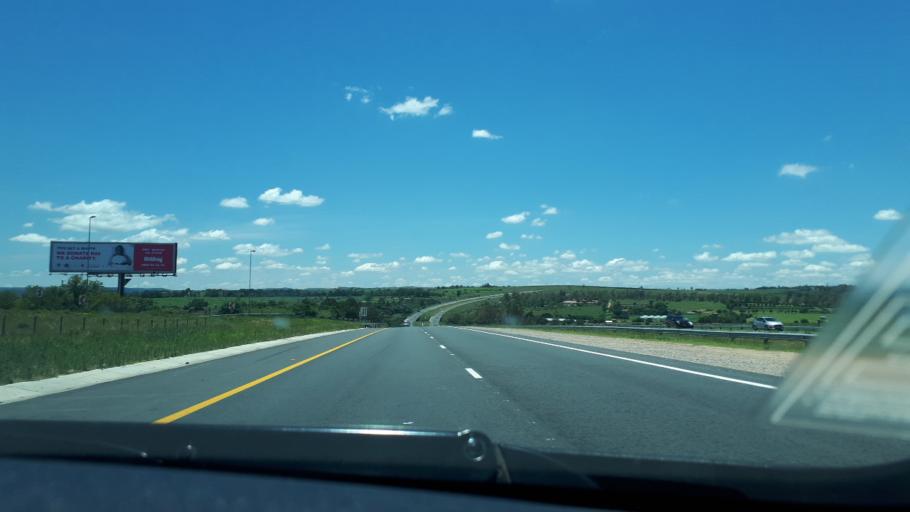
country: ZA
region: Gauteng
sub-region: City of Johannesburg Metropolitan Municipality
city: Diepsloot
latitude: -25.9579
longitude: 27.9519
